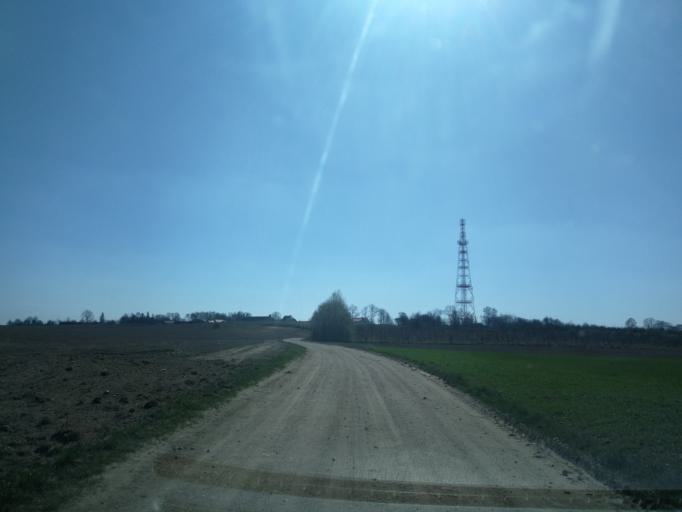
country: PL
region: Warmian-Masurian Voivodeship
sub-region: Powiat ostrodzki
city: Dabrowno
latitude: 53.4415
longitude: 19.9789
